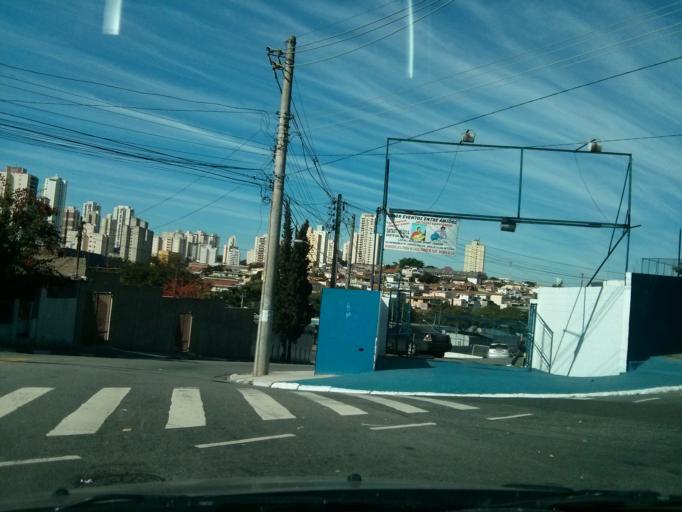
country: BR
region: Sao Paulo
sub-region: Sao Caetano Do Sul
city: Sao Caetano do Sul
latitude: -23.6168
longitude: -46.6110
